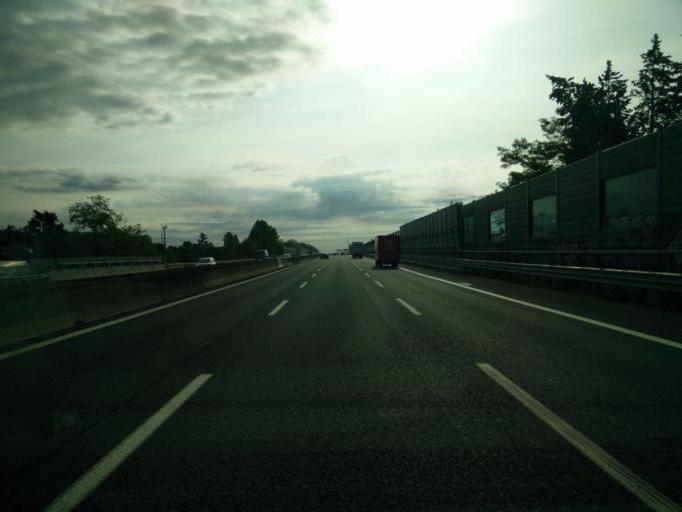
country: IT
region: Lombardy
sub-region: Provincia di Brescia
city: Roncadelle
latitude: 45.5290
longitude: 10.1574
